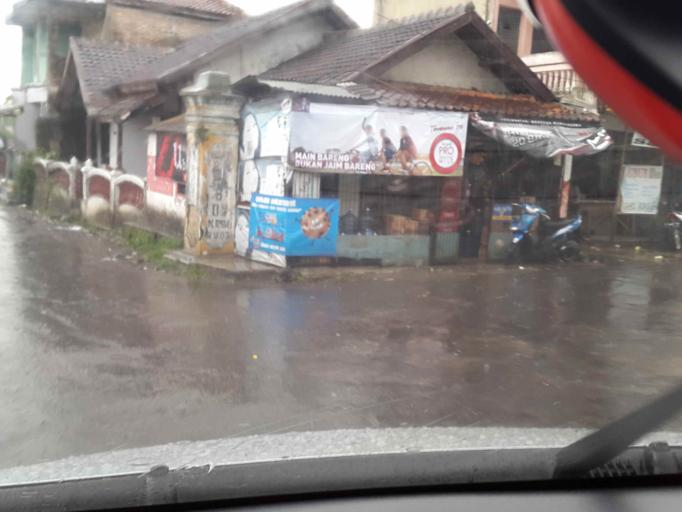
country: ID
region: West Java
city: Sukabumi
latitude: -6.9017
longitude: 106.9267
